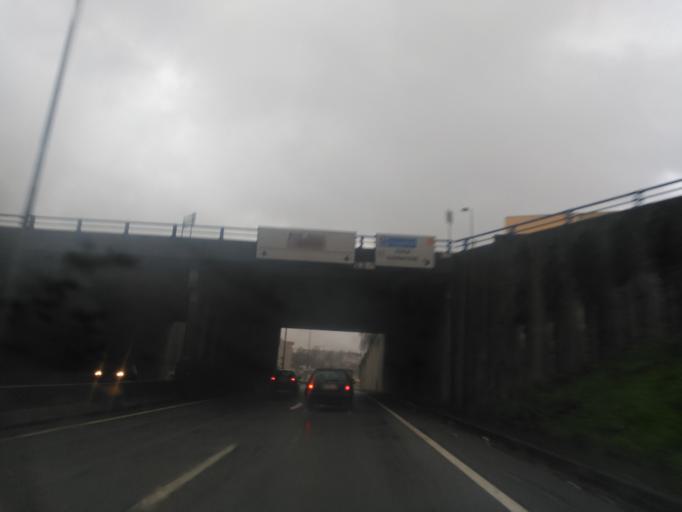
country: PT
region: Braga
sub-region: Braga
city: Braga
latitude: 41.5620
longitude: -8.4133
